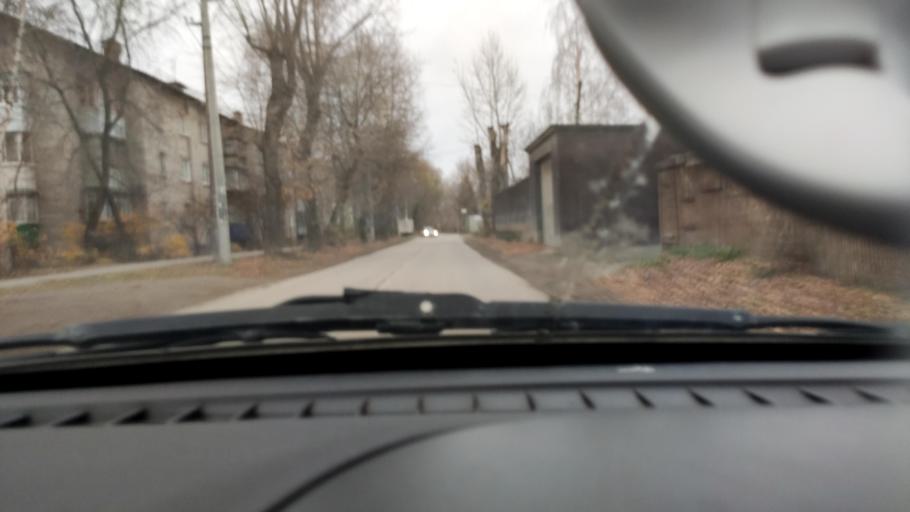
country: RU
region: Perm
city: Kondratovo
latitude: 58.0041
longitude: 56.1179
